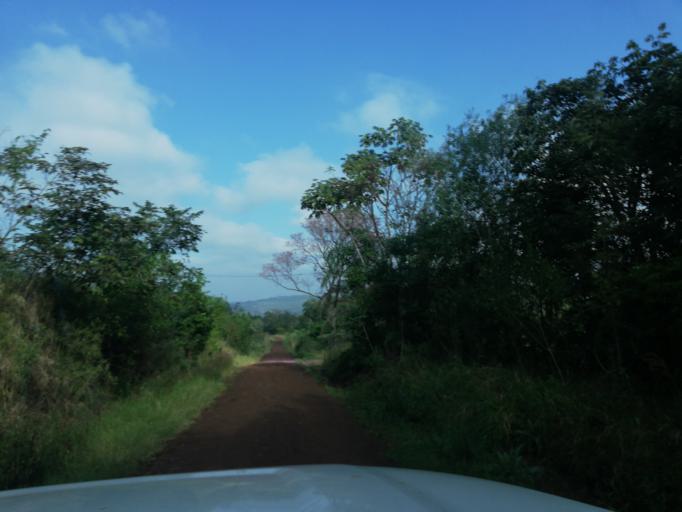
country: AR
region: Misiones
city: Cerro Azul
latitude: -27.5817
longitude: -55.5165
